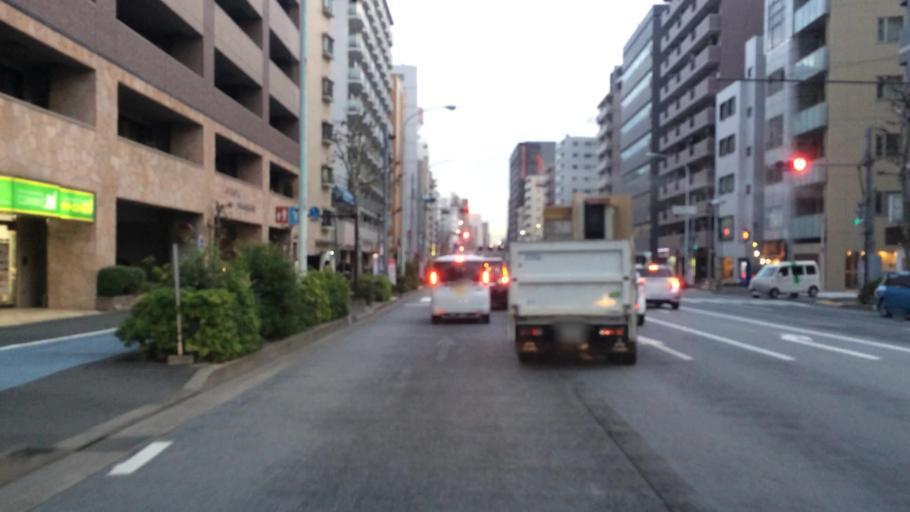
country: JP
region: Tokyo
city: Tokyo
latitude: 35.6388
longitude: 139.7040
